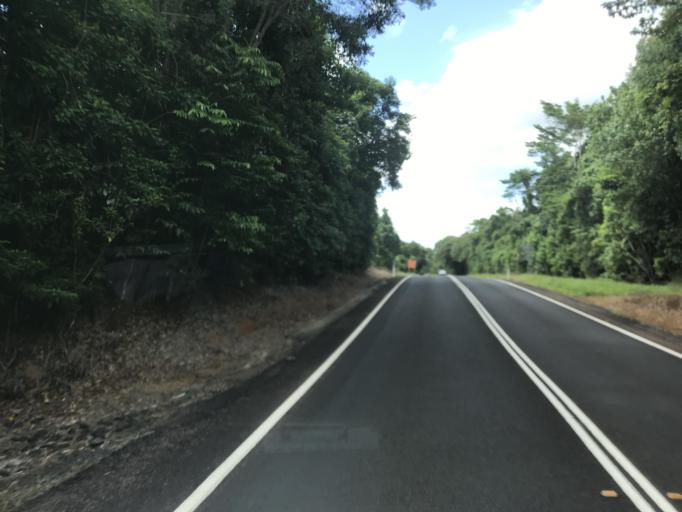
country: AU
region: Queensland
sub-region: Cassowary Coast
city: Innisfail
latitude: -17.8574
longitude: 146.0655
